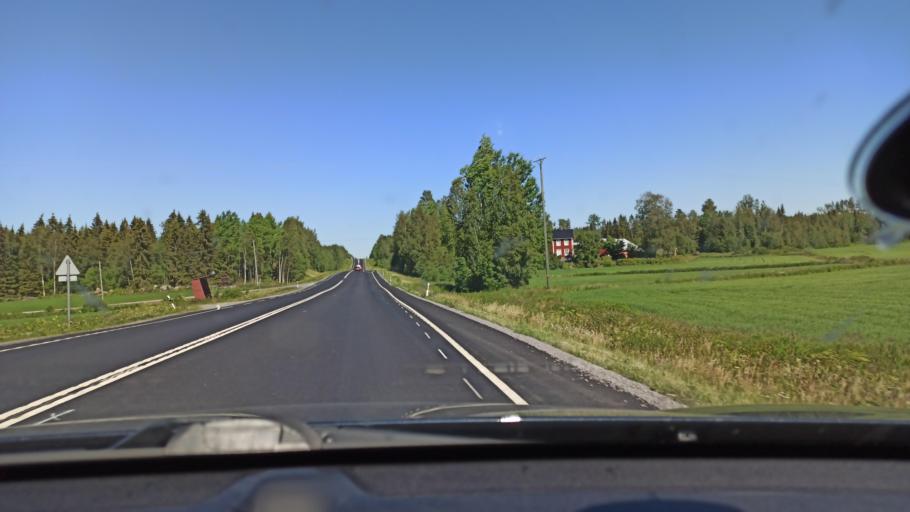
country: FI
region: Ostrobothnia
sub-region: Vaasa
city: Oravais
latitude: 63.2671
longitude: 22.2969
